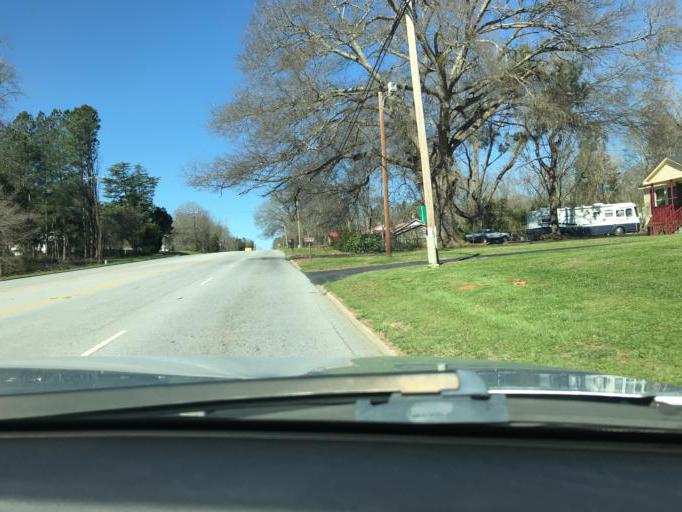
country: US
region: South Carolina
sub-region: Laurens County
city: Watts Mills
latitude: 34.4889
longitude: -81.9640
